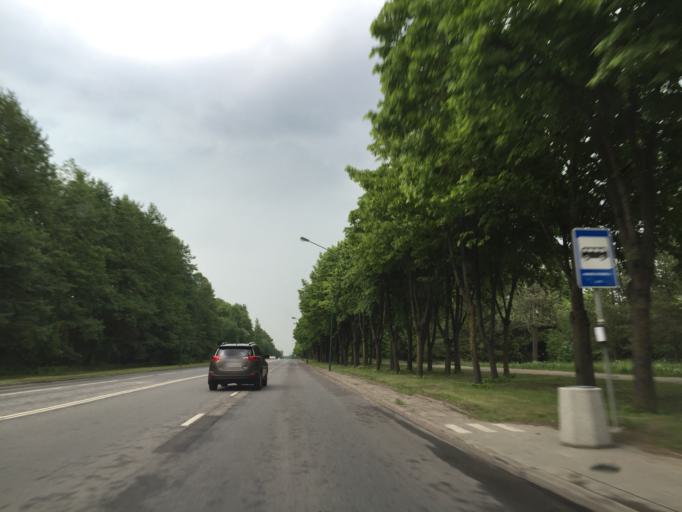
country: LT
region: Klaipedos apskritis
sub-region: Klaipeda
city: Klaipeda
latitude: 55.7369
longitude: 21.1298
